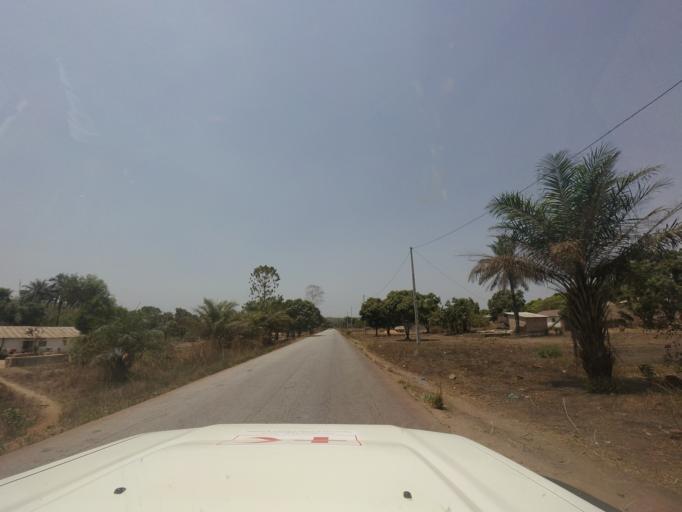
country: GN
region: Kindia
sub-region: Coyah
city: Coyah
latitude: 9.8302
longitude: -13.1115
